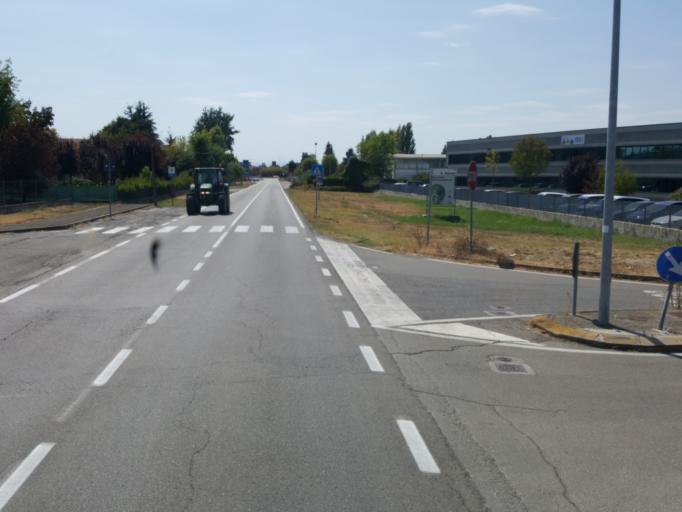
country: IT
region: Emilia-Romagna
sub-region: Provincia di Reggio Emilia
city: Novellara
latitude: 44.8560
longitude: 10.7409
